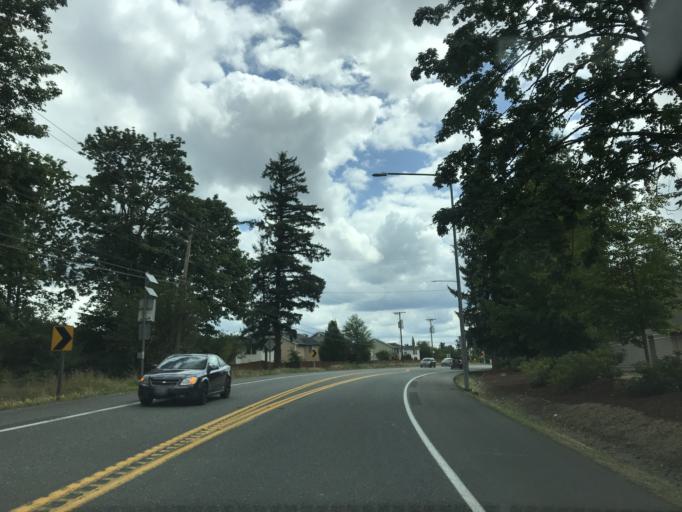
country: US
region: Washington
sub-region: King County
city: Maple Heights-Lake Desire
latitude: 47.4389
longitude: -122.1181
